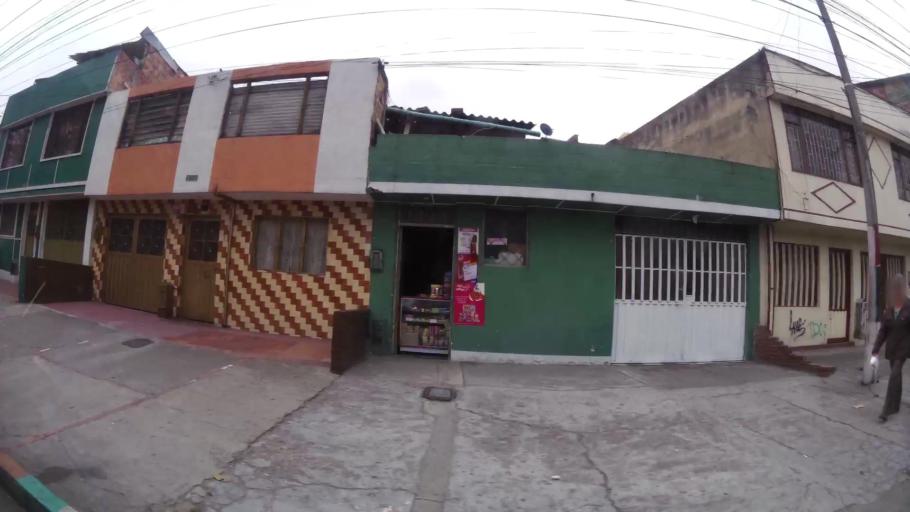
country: CO
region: Bogota D.C.
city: Bogota
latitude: 4.5909
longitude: -74.1001
